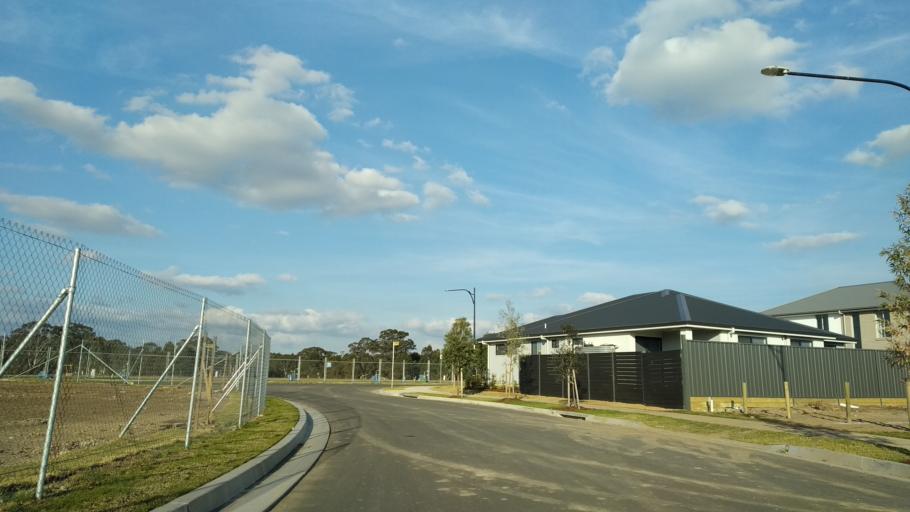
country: AU
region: New South Wales
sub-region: Penrith Municipality
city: Werrington County
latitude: -33.7308
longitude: 150.7553
